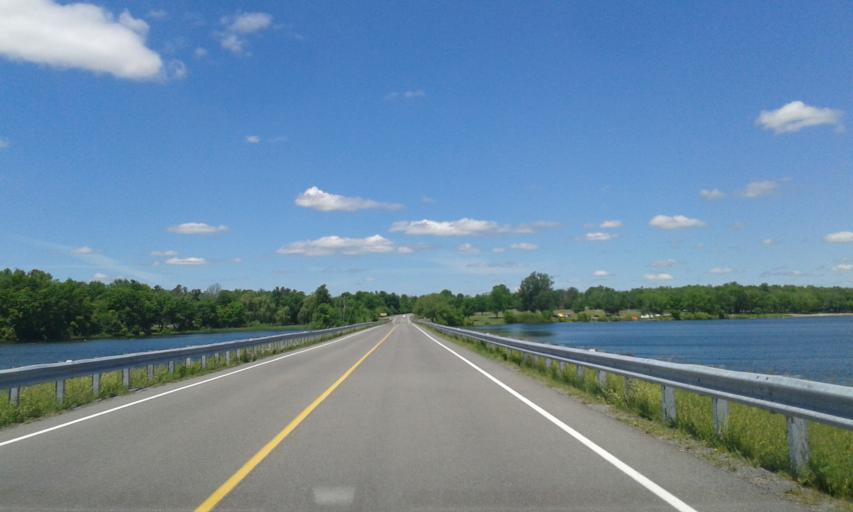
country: US
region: New York
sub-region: St. Lawrence County
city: Massena
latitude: 45.0073
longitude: -74.8944
